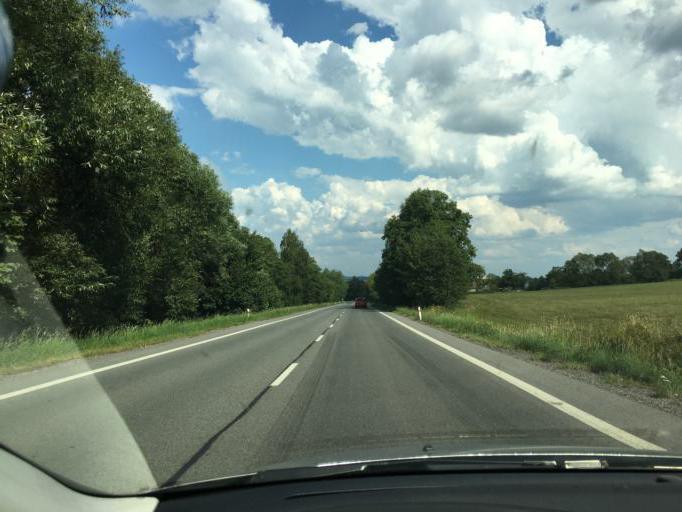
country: CZ
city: Horni Branna
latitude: 50.6201
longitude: 15.5809
